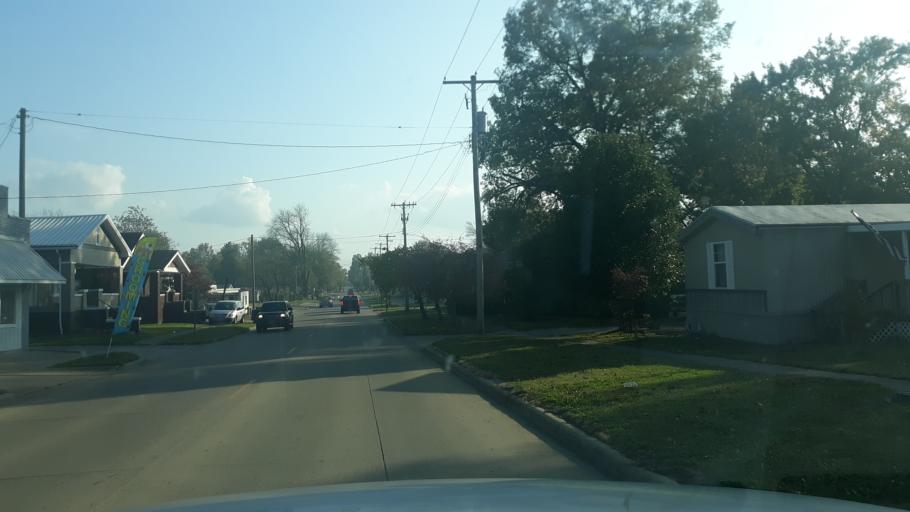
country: US
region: Illinois
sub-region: Saline County
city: Harrisburg
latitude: 37.7343
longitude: -88.5404
